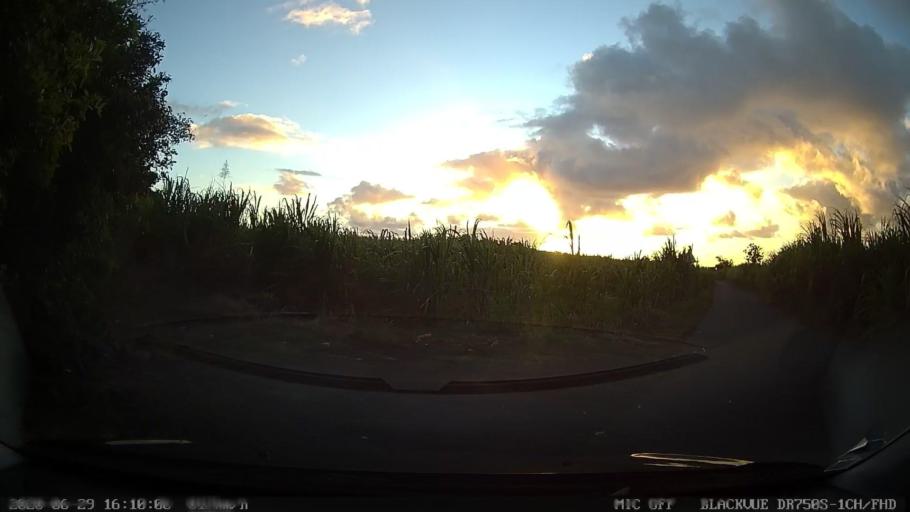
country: RE
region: Reunion
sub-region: Reunion
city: Bras-Panon
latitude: -20.9916
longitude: 55.6849
